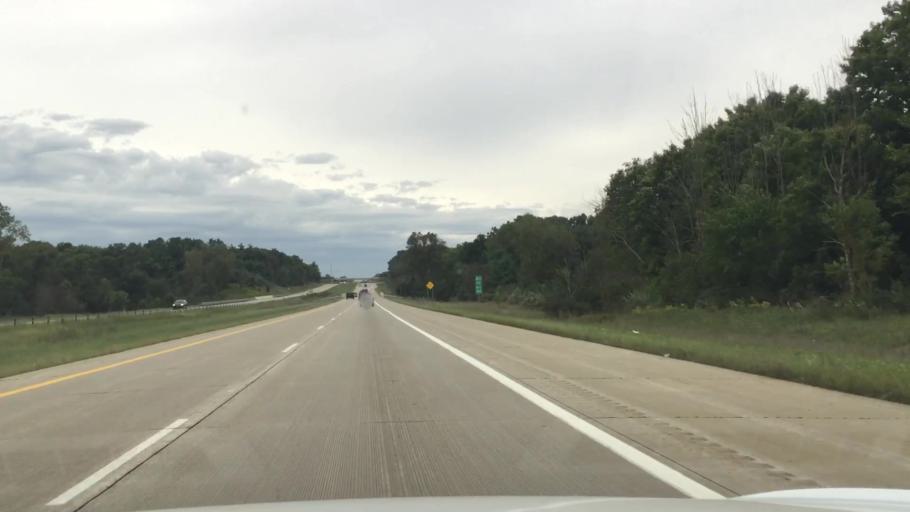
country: US
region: Michigan
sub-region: Saint Clair County
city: Marysville
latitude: 42.8716
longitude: -82.5447
